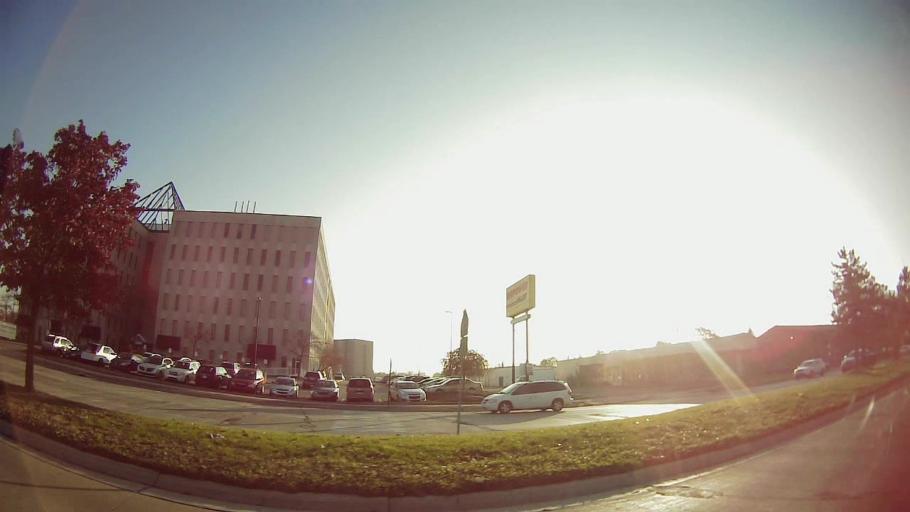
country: US
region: Michigan
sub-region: Oakland County
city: Southfield
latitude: 42.4799
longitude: -83.2022
